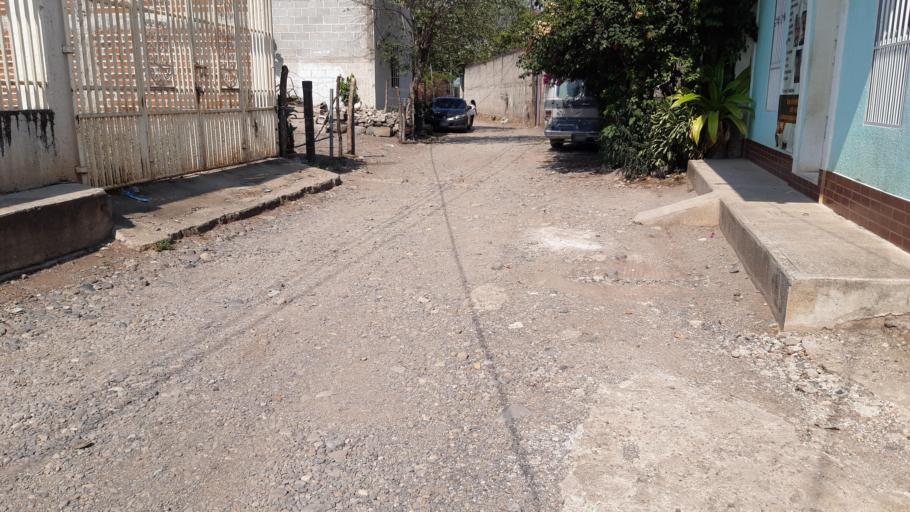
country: GT
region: Jutiapa
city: Asuncion Mita
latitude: 14.2843
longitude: -89.7233
